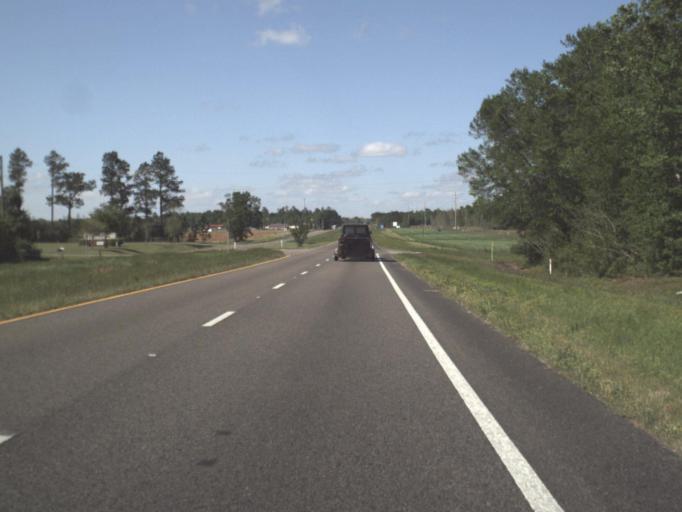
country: US
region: Florida
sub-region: Escambia County
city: Molino
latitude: 30.7234
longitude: -87.3494
